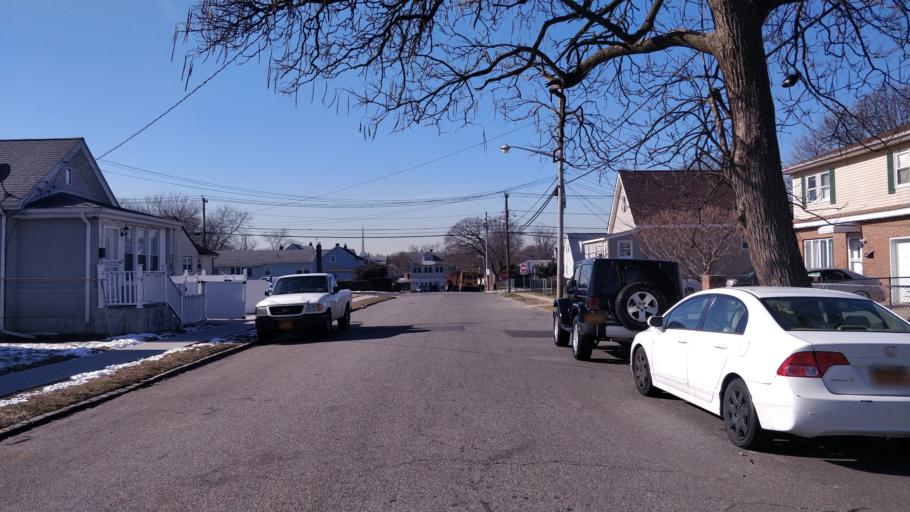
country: US
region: New York
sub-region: Nassau County
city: New Cassel
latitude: 40.7601
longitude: -73.5747
